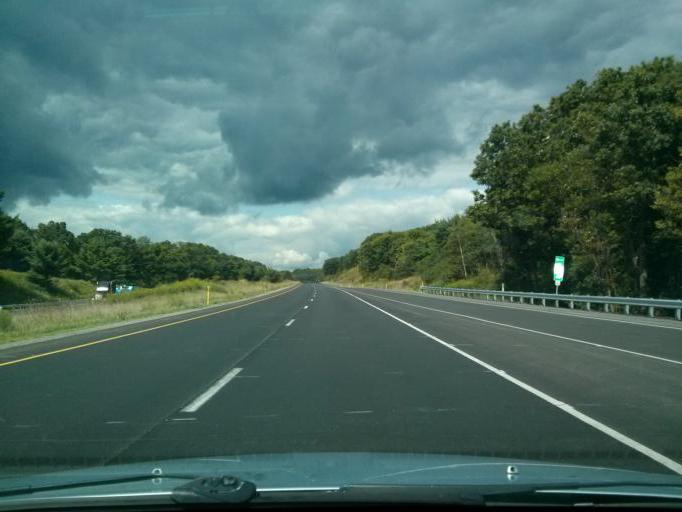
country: US
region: Pennsylvania
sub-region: Clarion County
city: Clarion
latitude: 41.1941
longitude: -79.4301
